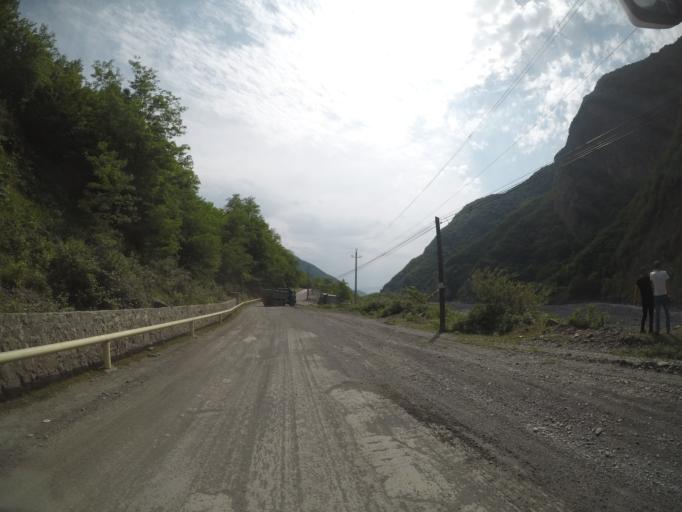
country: AZ
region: Qakh Rayon
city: Qaxbas
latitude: 41.4630
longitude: 47.0324
